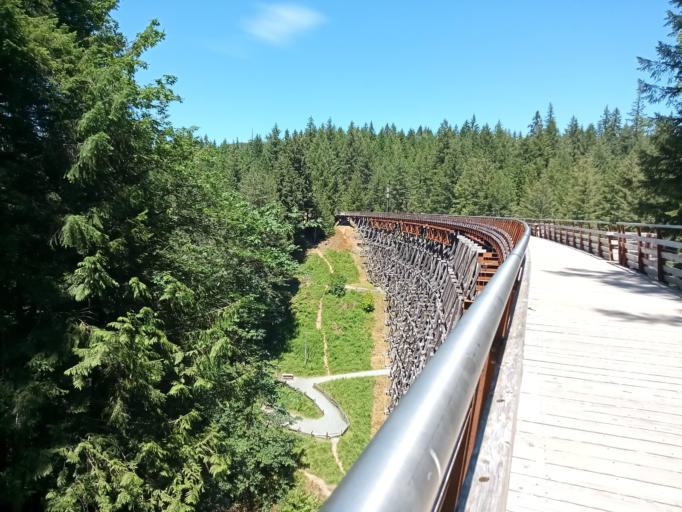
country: CA
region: British Columbia
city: Duncan
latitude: 48.6681
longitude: -123.6941
